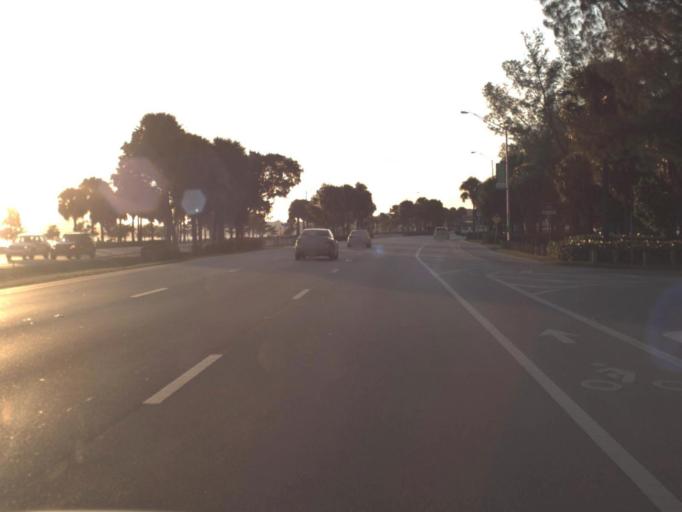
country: US
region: Florida
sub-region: Miami-Dade County
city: Miami
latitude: 25.7461
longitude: -80.1959
